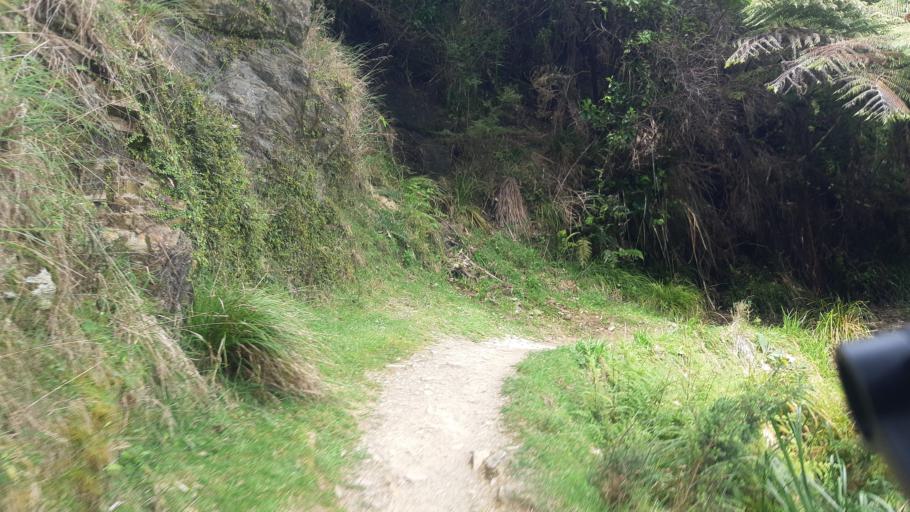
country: NZ
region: Marlborough
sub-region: Marlborough District
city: Picton
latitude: -41.2469
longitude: 173.9587
